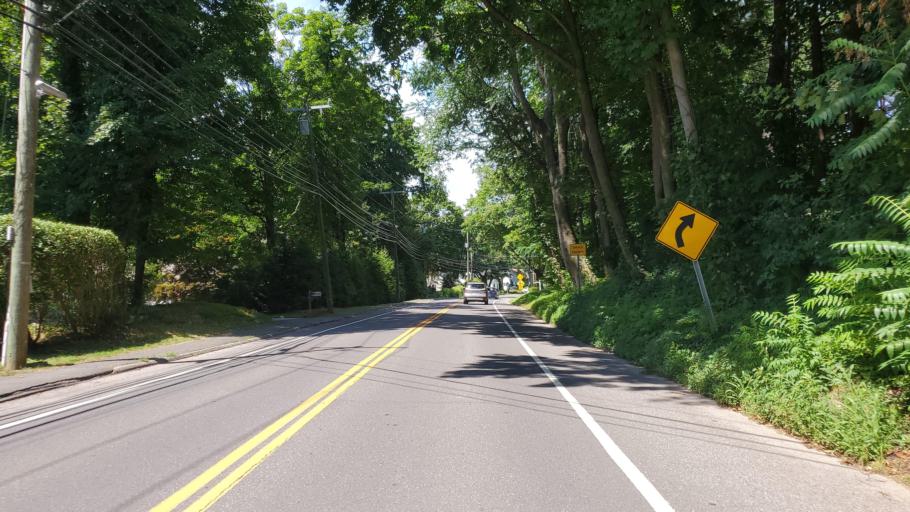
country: US
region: Connecticut
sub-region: Fairfield County
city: Westport
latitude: 41.1175
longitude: -73.3620
